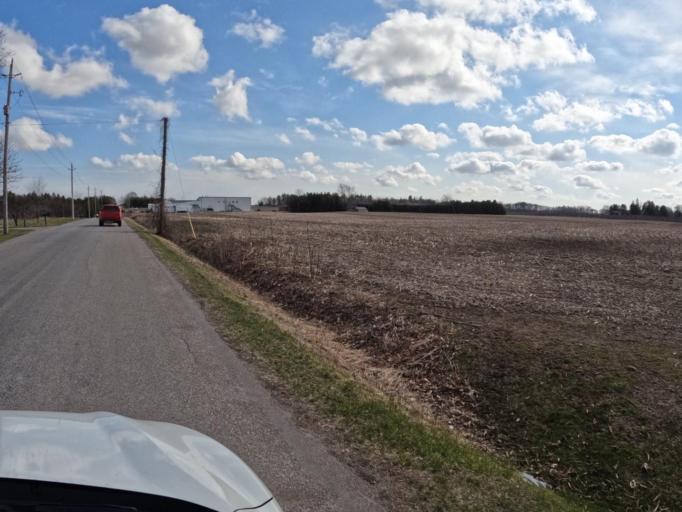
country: CA
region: Ontario
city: Norfolk County
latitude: 42.8663
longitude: -80.2761
